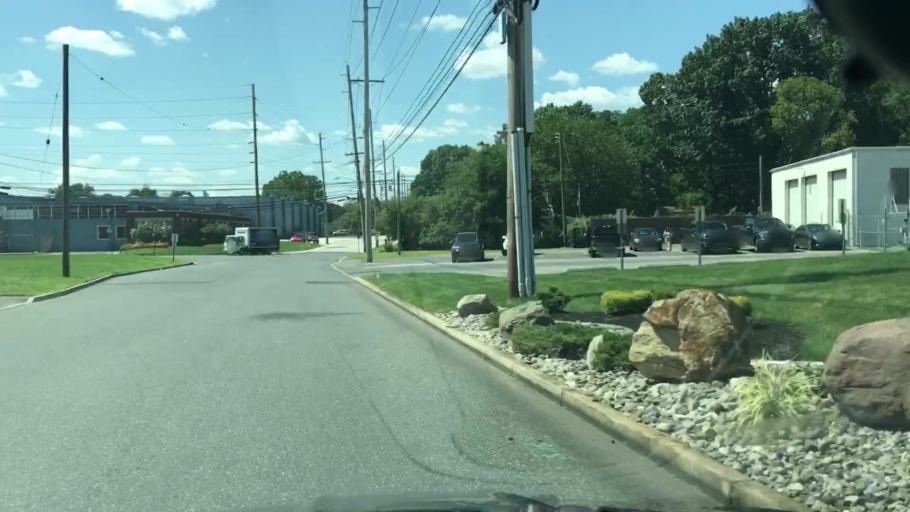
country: US
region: New Jersey
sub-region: Camden County
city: Pennsauken
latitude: 39.9799
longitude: -75.0431
